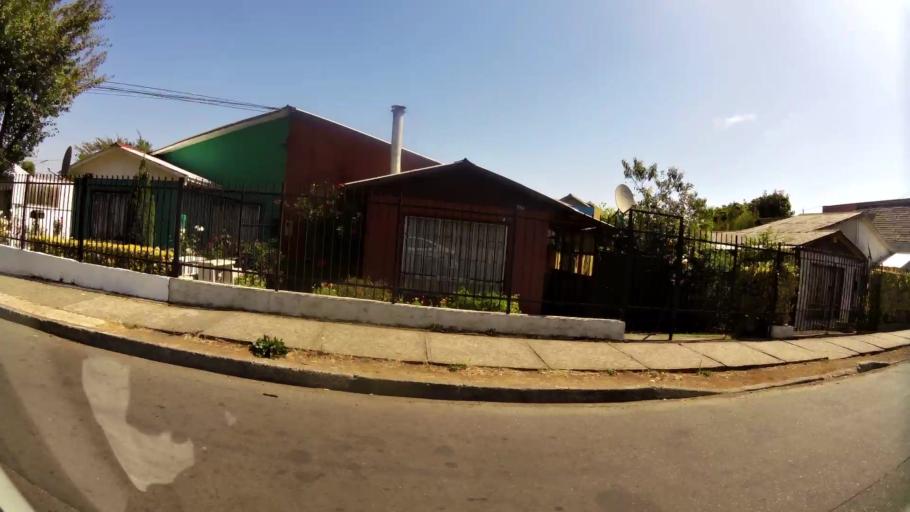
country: CL
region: Biobio
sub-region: Provincia de Concepcion
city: Concepcion
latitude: -36.7898
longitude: -73.0424
